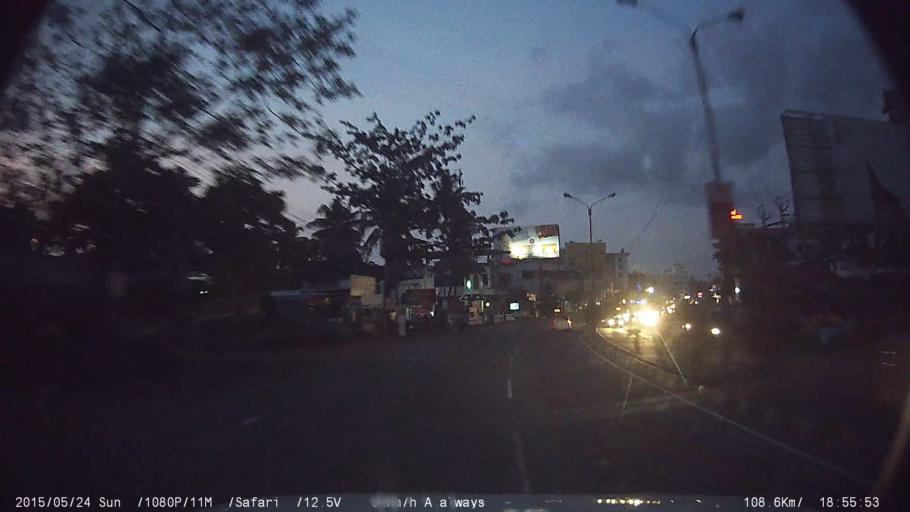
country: IN
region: Kerala
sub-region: Ernakulam
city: Angamali
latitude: 10.1819
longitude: 76.3796
